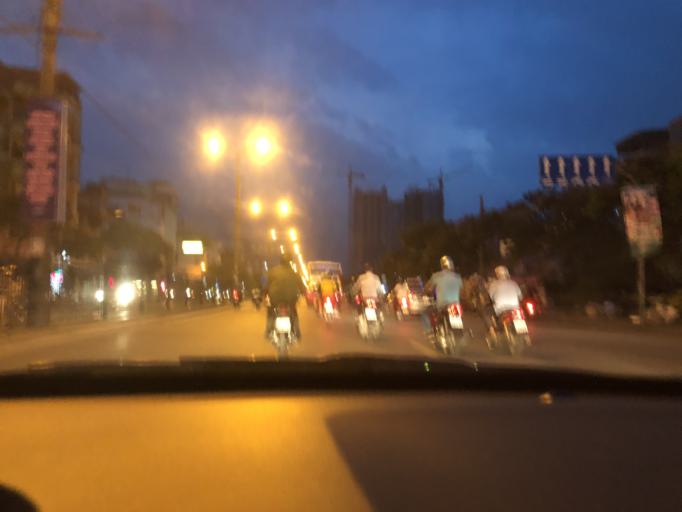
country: VN
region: Ha Noi
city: Hai BaTrung
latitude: 20.9910
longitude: 105.8411
